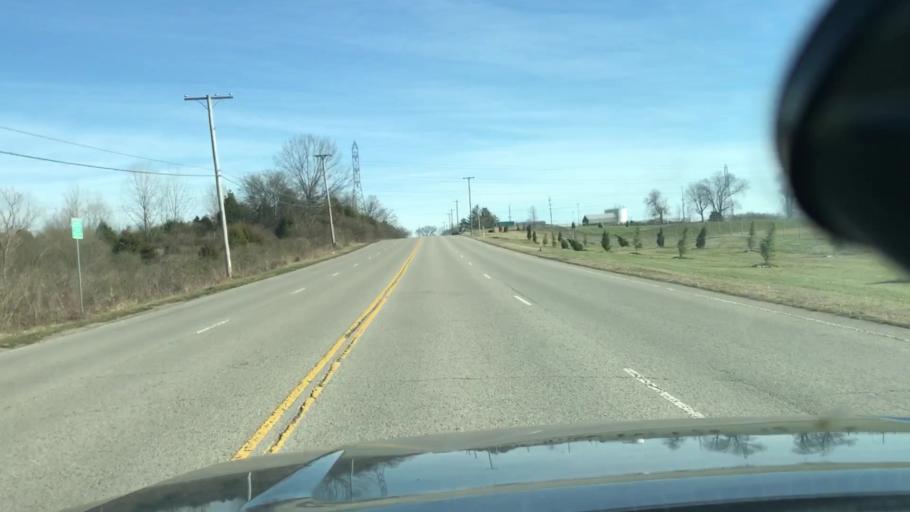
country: US
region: Tennessee
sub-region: Davidson County
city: Nashville
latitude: 36.1851
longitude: -86.8559
